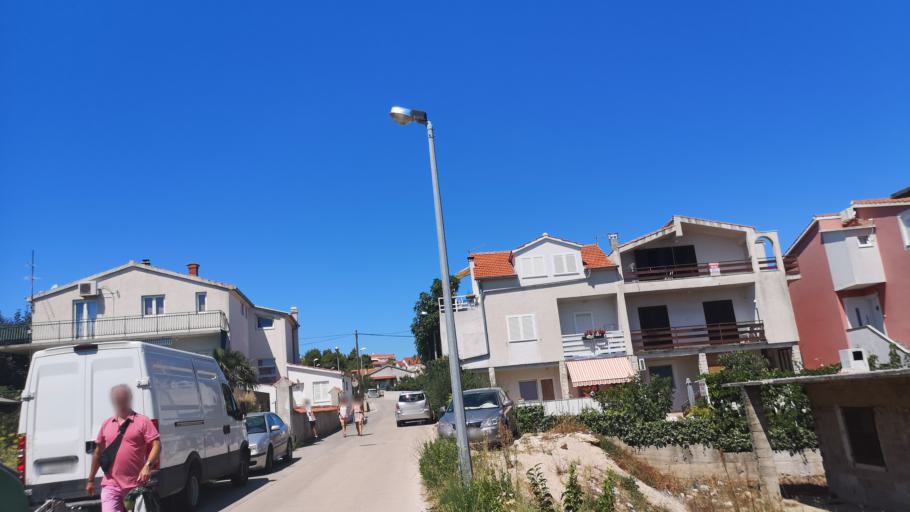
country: HR
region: Sibensko-Kniniska
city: Vodice
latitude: 43.7627
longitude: 15.7694
